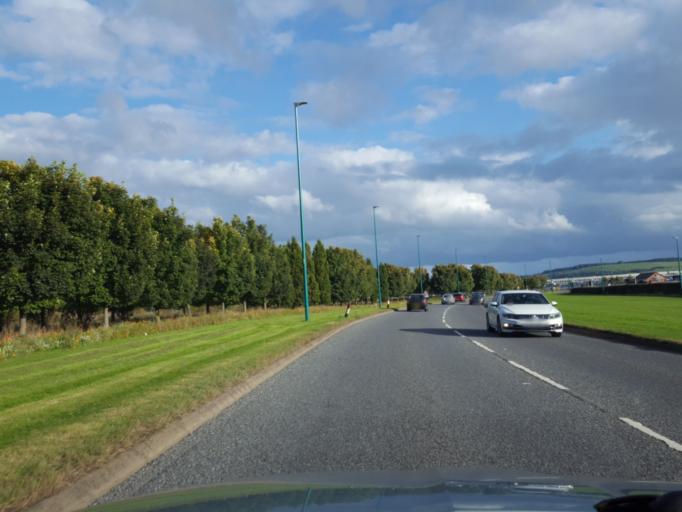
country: GB
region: Scotland
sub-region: Dundee City
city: Dundee
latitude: 56.4542
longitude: -3.0024
